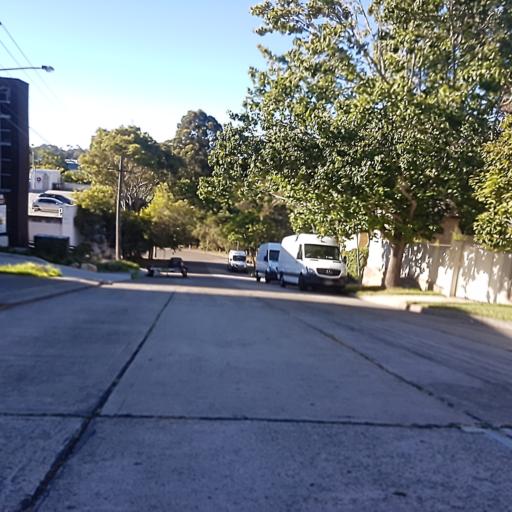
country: AU
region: New South Wales
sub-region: Willoughby
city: Castle Cove
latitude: -33.7900
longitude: 151.2029
